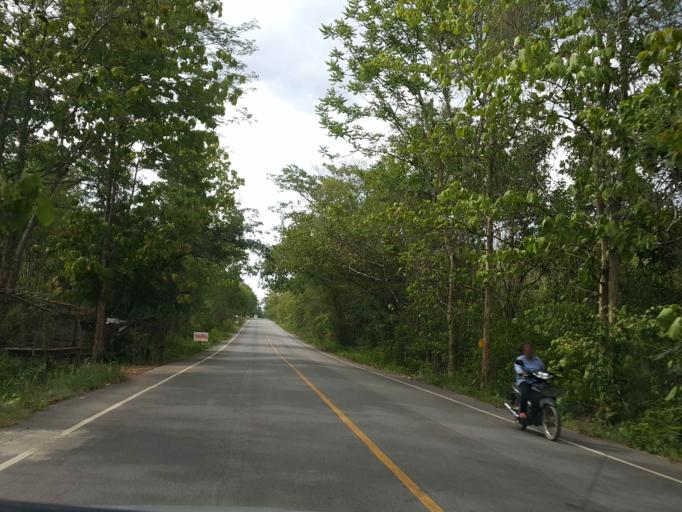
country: TH
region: Sukhothai
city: Thung Saliam
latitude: 17.3849
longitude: 99.3989
